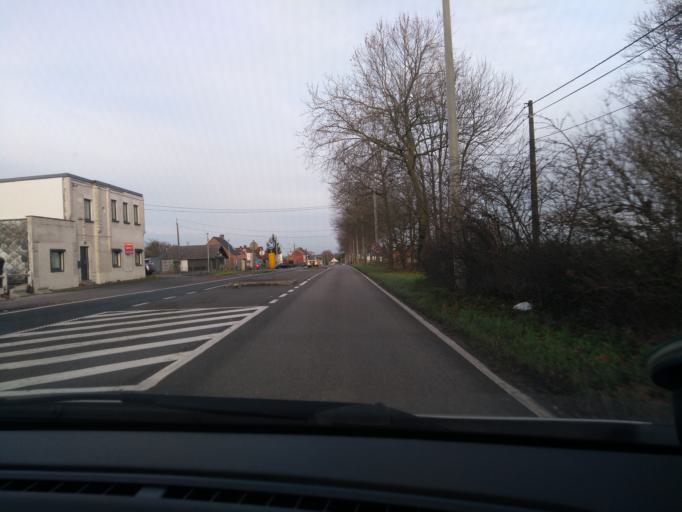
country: BE
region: Wallonia
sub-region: Province du Hainaut
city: Quevy-le-Petit
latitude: 50.3519
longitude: 3.9679
